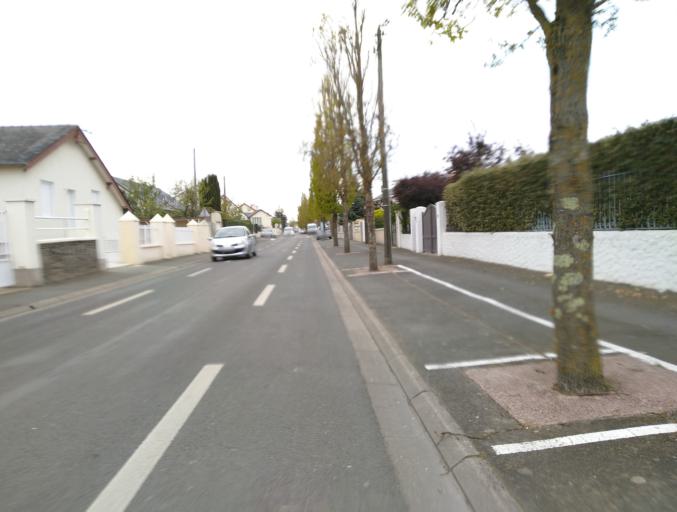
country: FR
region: Pays de la Loire
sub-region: Departement de Maine-et-Loire
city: Les Ponts-de-Ce
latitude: 47.4470
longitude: -0.5187
